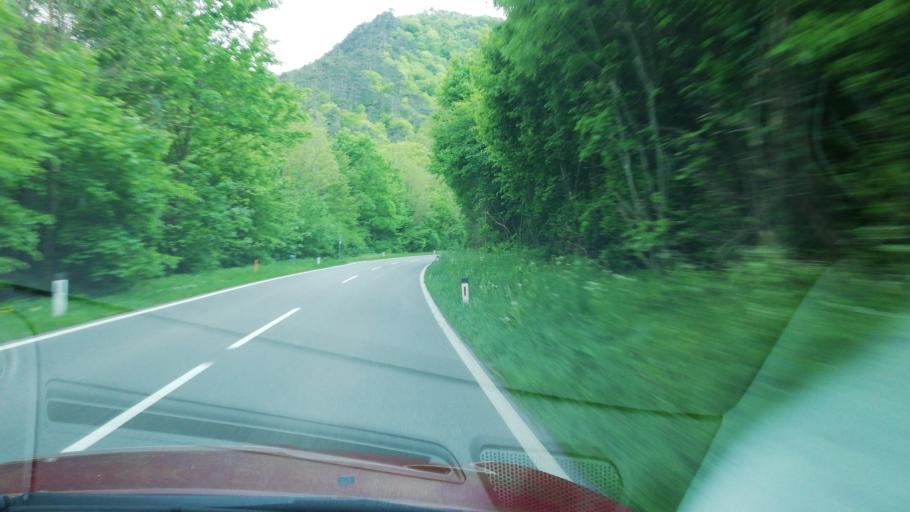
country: AT
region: Lower Austria
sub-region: Politischer Bezirk Modling
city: Gaaden
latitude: 48.0128
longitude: 16.1680
